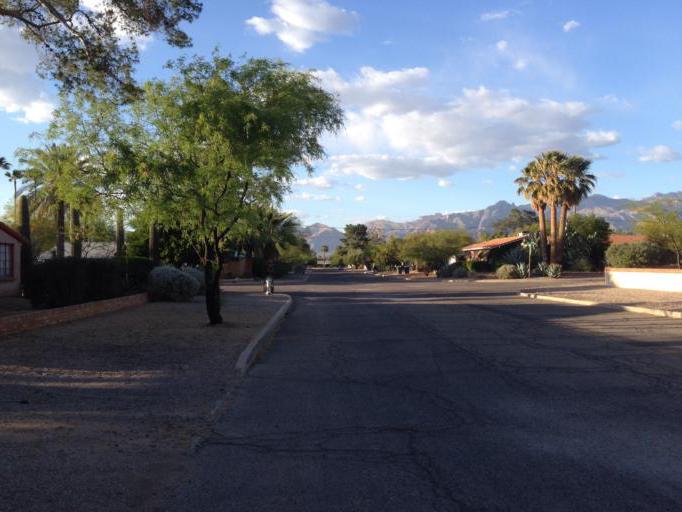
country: US
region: Arizona
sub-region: Pima County
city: Tucson
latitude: 32.2462
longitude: -110.9386
